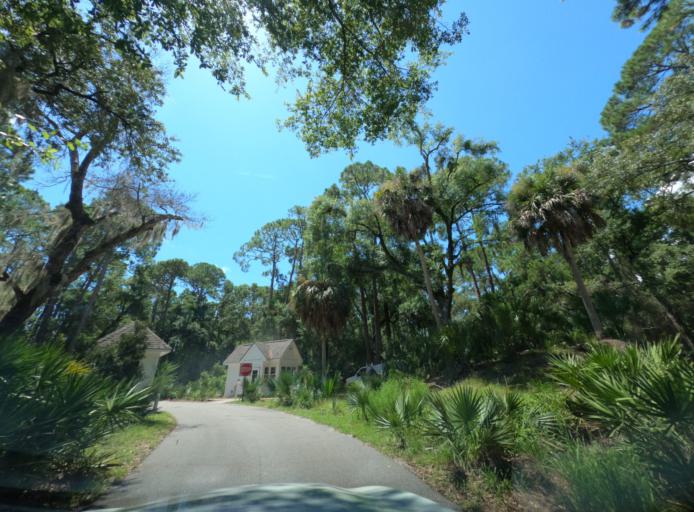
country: US
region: South Carolina
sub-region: Beaufort County
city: Beaufort
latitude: 32.3593
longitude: -80.4477
